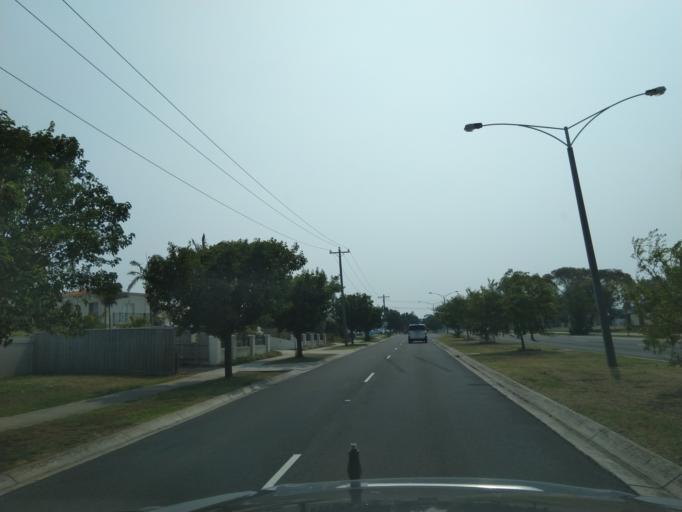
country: AU
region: Victoria
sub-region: Hume
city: Attwood
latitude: -37.6533
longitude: 144.8865
